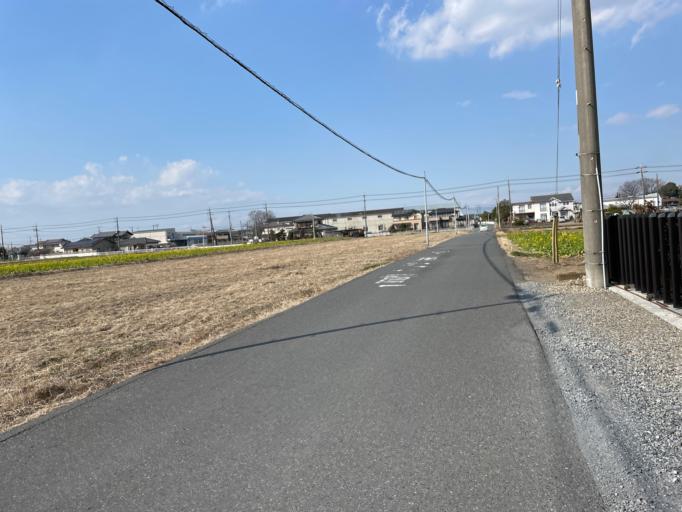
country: JP
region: Saitama
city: Yorii
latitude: 36.1220
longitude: 139.2347
